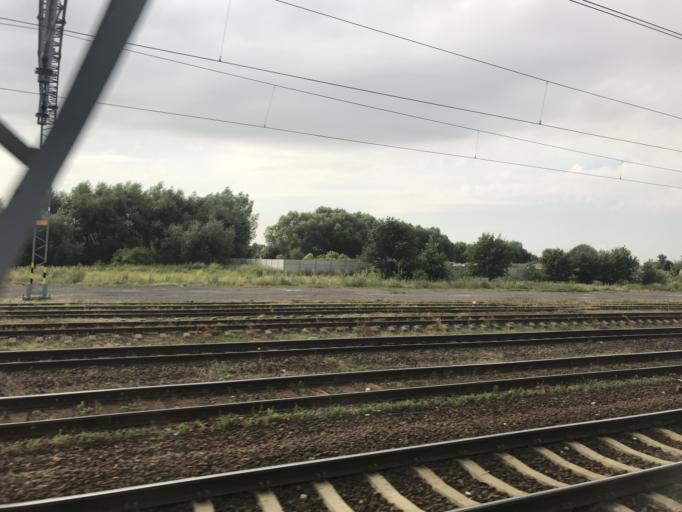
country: PL
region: Pomeranian Voivodeship
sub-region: Powiat tczewski
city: Pelplin
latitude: 53.9283
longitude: 18.7100
